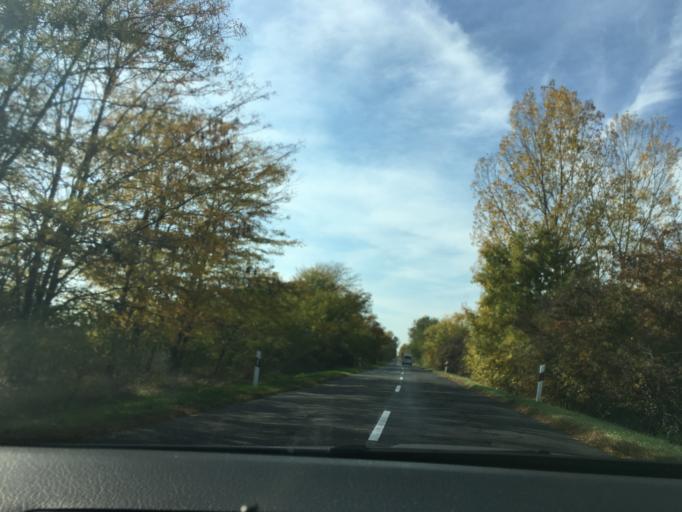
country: HU
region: Hajdu-Bihar
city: Nyirabrany
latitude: 47.5267
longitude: 21.9693
